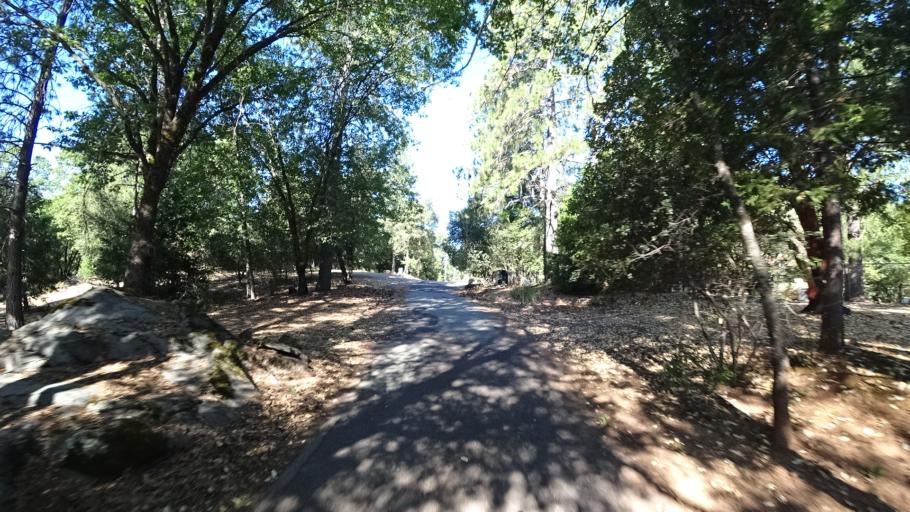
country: US
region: California
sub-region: Amador County
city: Pioneer
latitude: 38.4127
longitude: -120.5518
